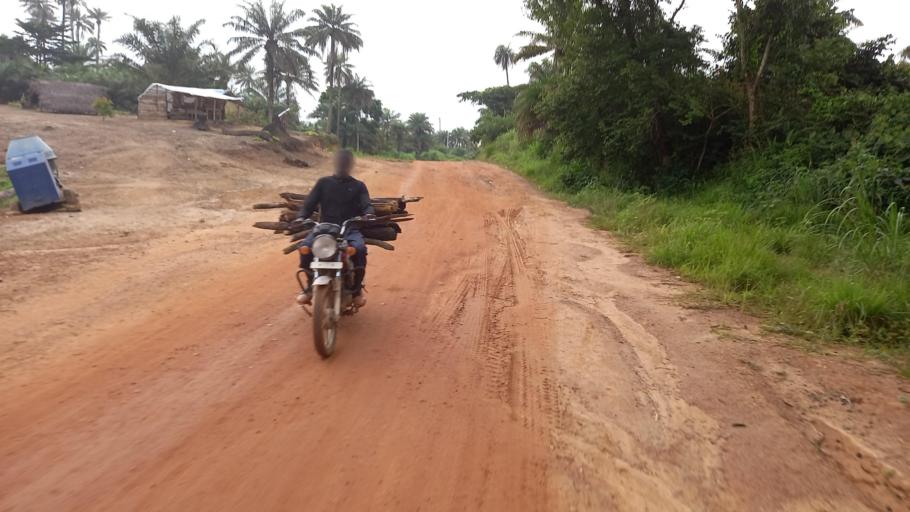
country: SL
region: Eastern Province
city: Kailahun
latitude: 8.2583
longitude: -10.5417
